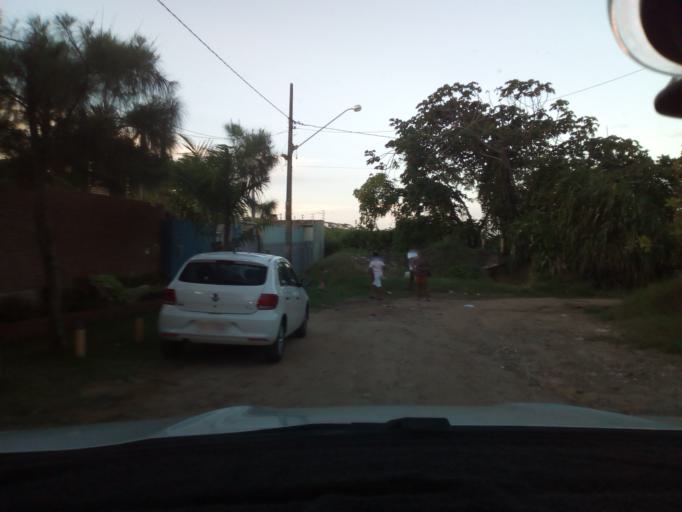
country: BR
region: Paraiba
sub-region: Joao Pessoa
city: Joao Pessoa
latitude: -7.1990
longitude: -34.7989
